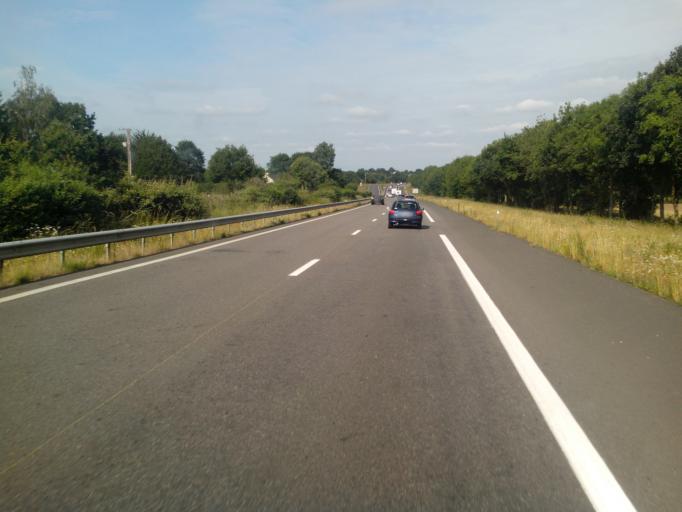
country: FR
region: Brittany
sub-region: Departement d'Ille-et-Vilaine
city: Saint-Thurial
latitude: 48.0421
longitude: -1.9470
